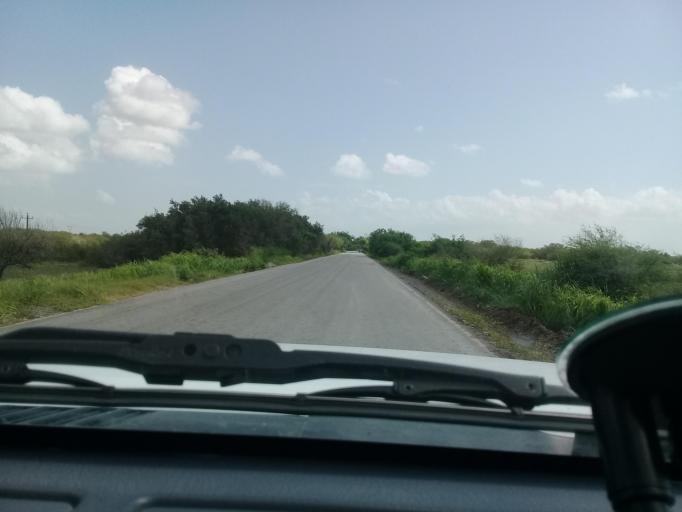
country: MX
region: Veracruz
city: Moralillo
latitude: 22.1844
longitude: -97.9464
